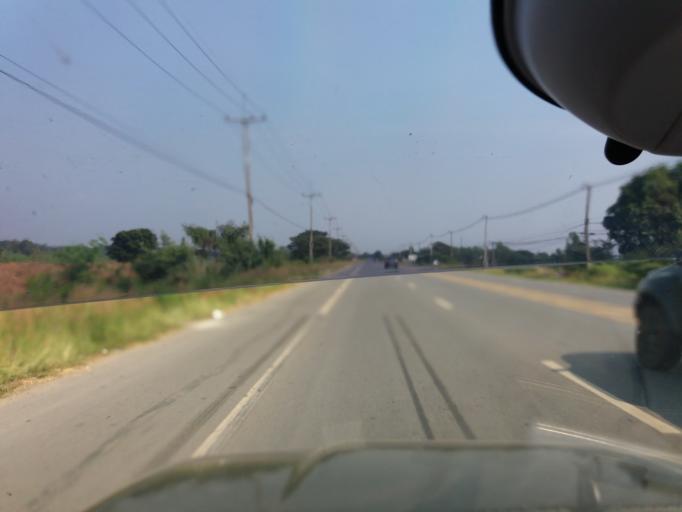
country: TH
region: Sing Buri
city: Bang Racham
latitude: 14.8829
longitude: 100.3378
